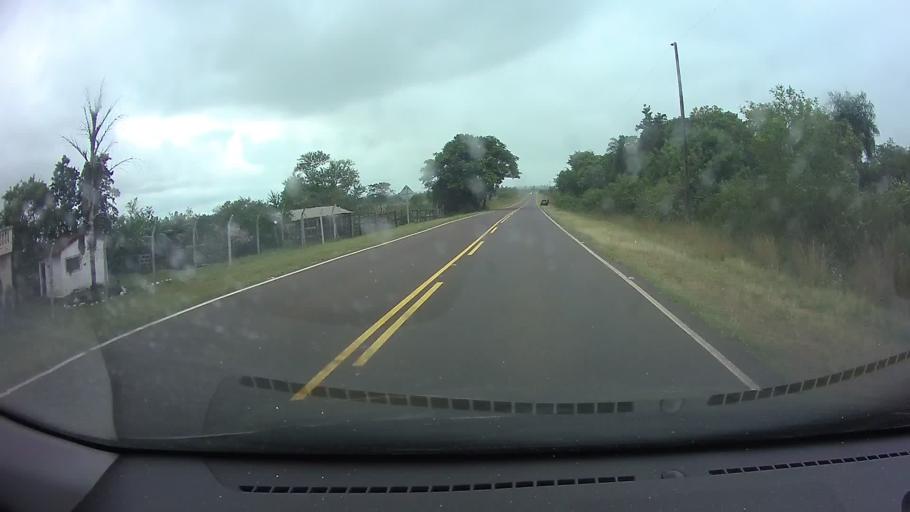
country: PY
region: Central
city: Nueva Italia
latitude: -25.6193
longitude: -57.4006
